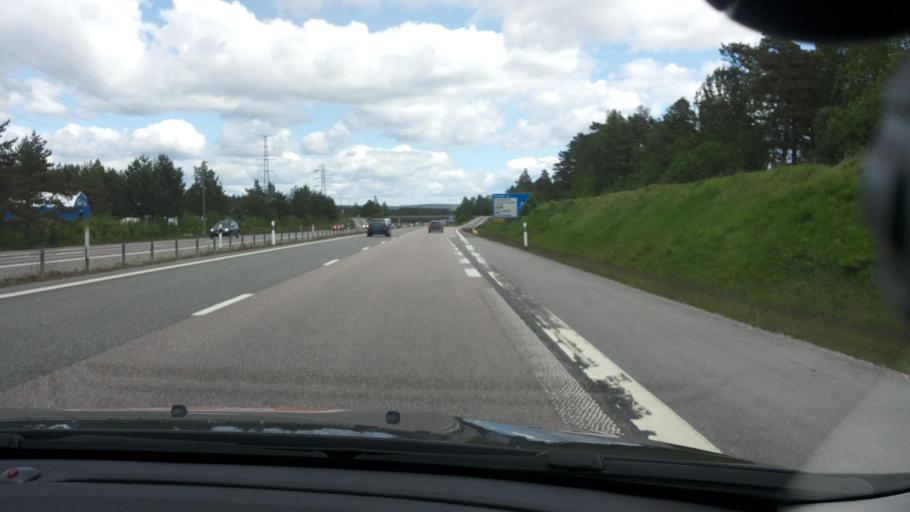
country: SE
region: Vaesternorrland
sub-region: Timra Kommun
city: Timra
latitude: 62.4923
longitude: 17.3287
